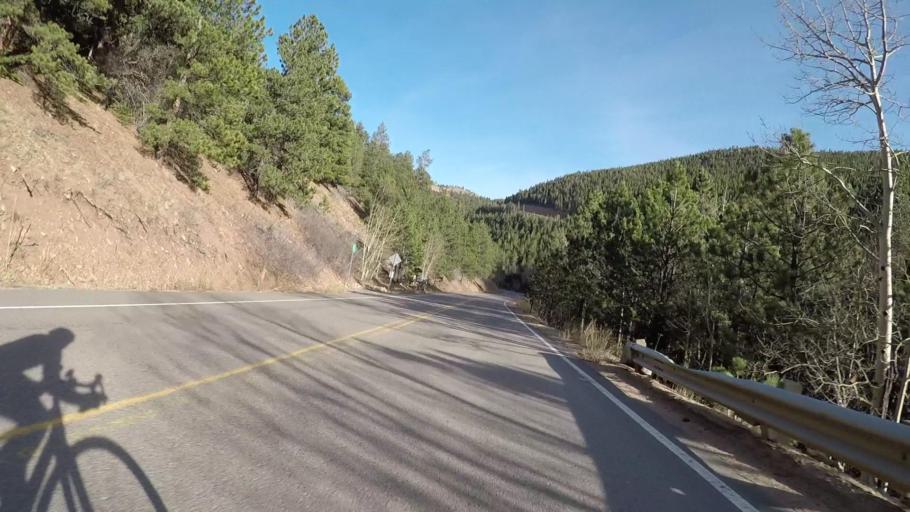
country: US
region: Colorado
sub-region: Boulder County
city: Nederland
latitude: 40.0561
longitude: -105.5007
